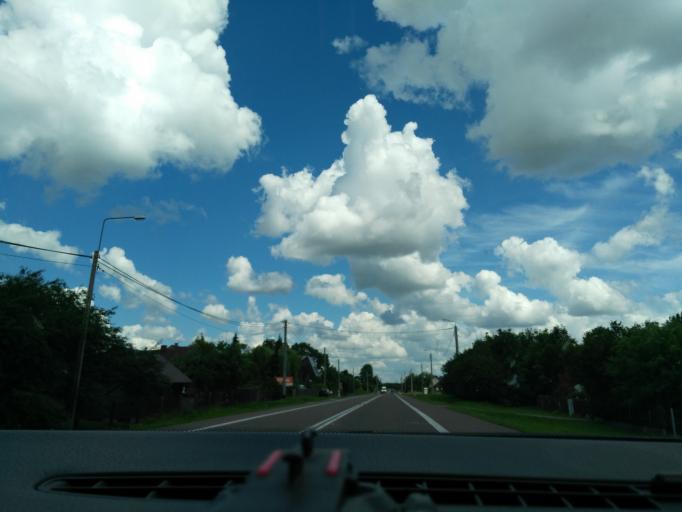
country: PL
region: Podlasie
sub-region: Powiat bielski
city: Bielsk Podlaski
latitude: 52.8005
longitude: 23.1921
